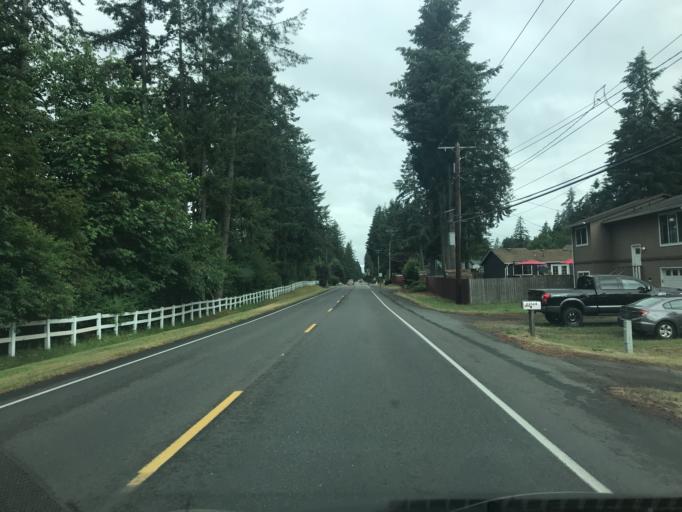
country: US
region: Washington
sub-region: King County
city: Black Diamond
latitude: 47.3435
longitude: -122.0272
